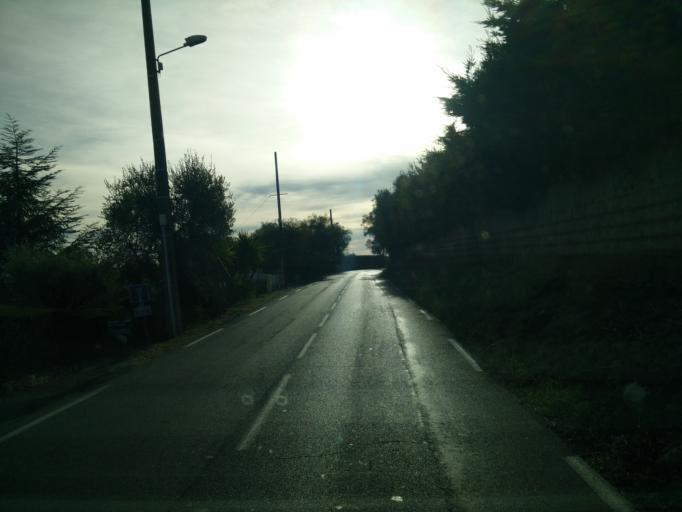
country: FR
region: Provence-Alpes-Cote d'Azur
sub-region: Departement des Alpes-Maritimes
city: Speracedes
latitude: 43.6437
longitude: 6.8509
